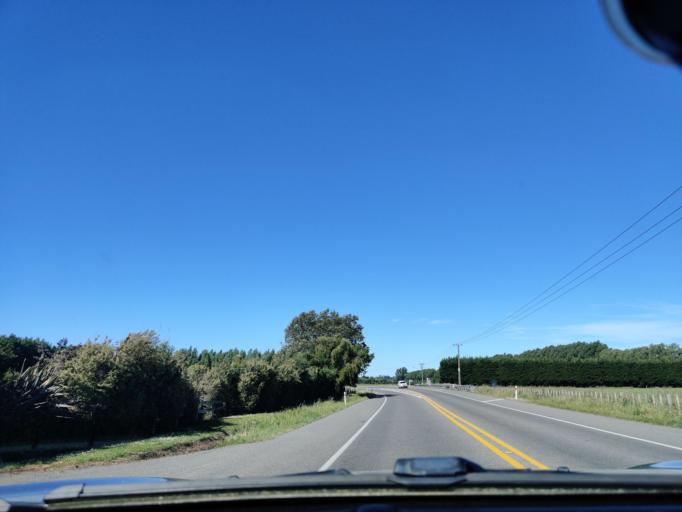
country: NZ
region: Wellington
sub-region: Masterton District
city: Masterton
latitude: -41.0652
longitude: 175.4858
